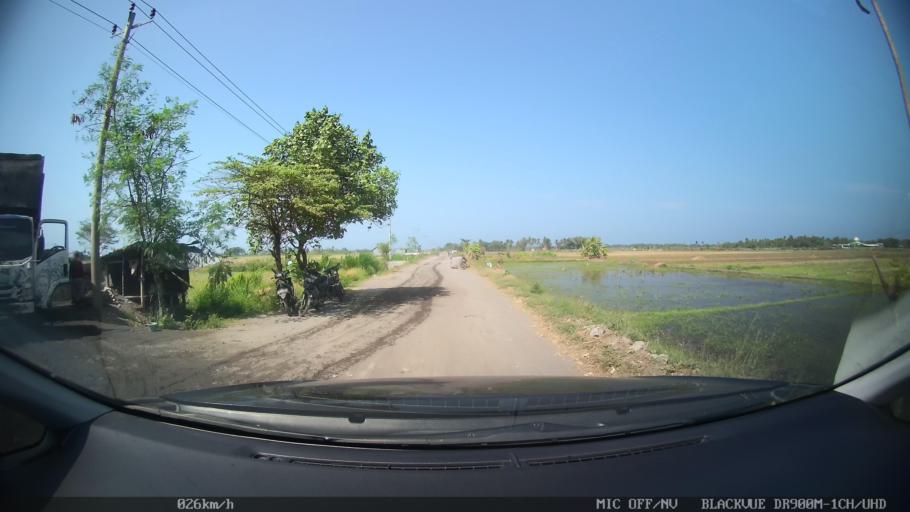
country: ID
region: Daerah Istimewa Yogyakarta
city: Srandakan
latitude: -7.9688
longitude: 110.2119
